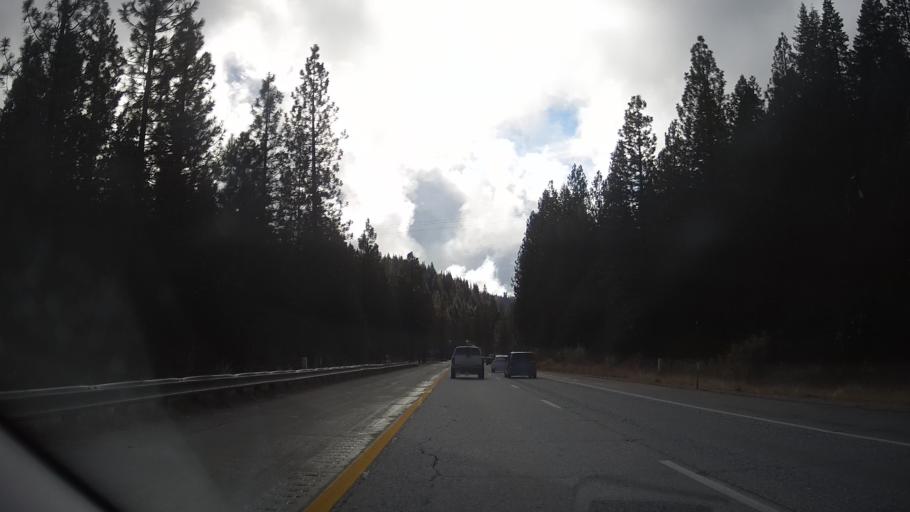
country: US
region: California
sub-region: Placer County
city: Foresthill
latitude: 39.2589
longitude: -120.7325
